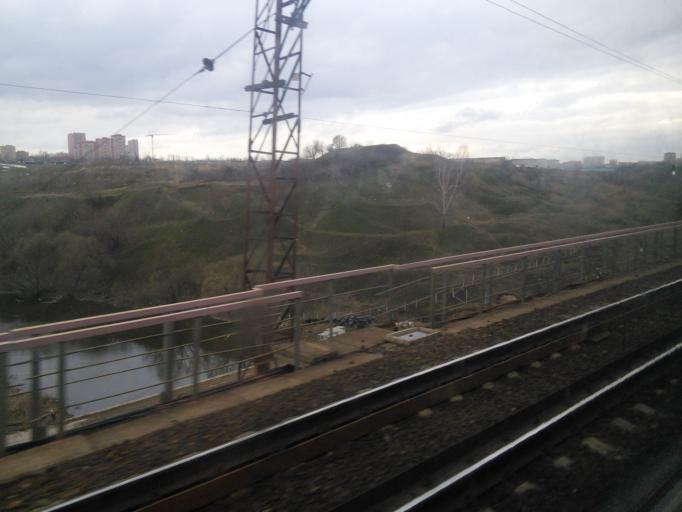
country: RU
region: Moskovskaya
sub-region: Podol'skiy Rayon
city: Podol'sk
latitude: 55.4492
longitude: 37.5662
